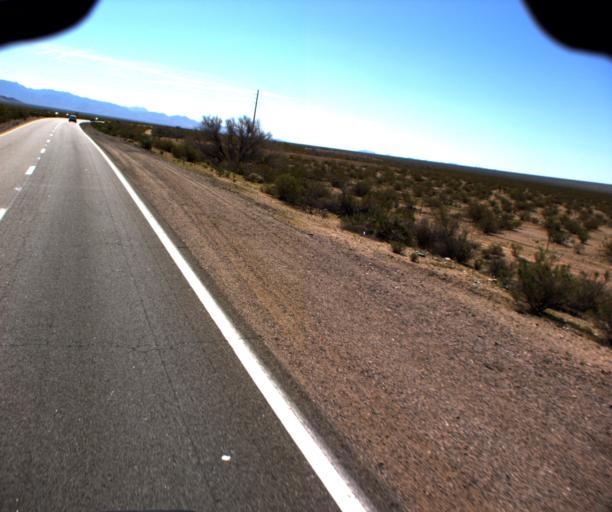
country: US
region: Arizona
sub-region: Mohave County
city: Dolan Springs
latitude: 35.6642
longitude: -114.4538
